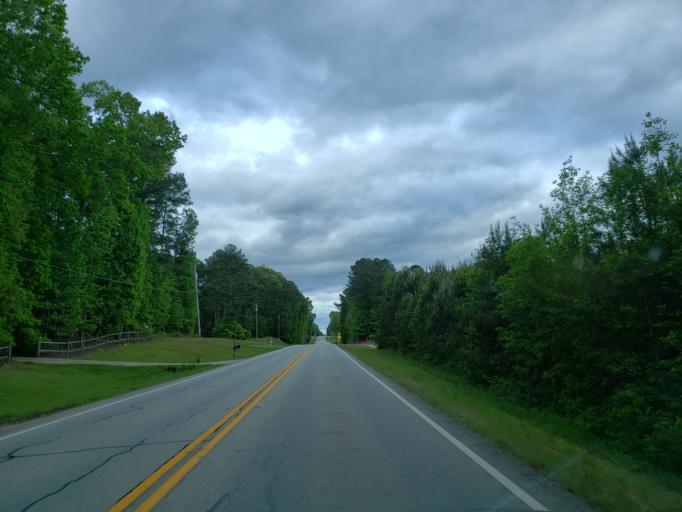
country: US
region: Georgia
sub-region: Haralson County
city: Buchanan
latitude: 33.8179
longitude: -85.0957
